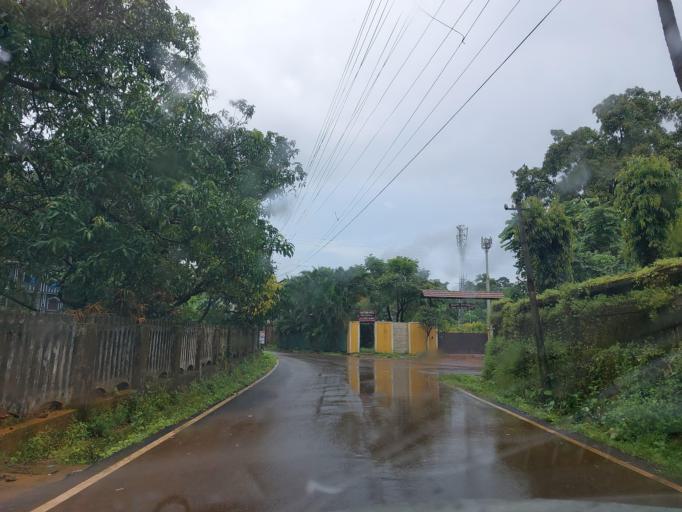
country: IN
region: Goa
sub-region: North Goa
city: Valpoy
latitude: 15.5301
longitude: 74.1313
